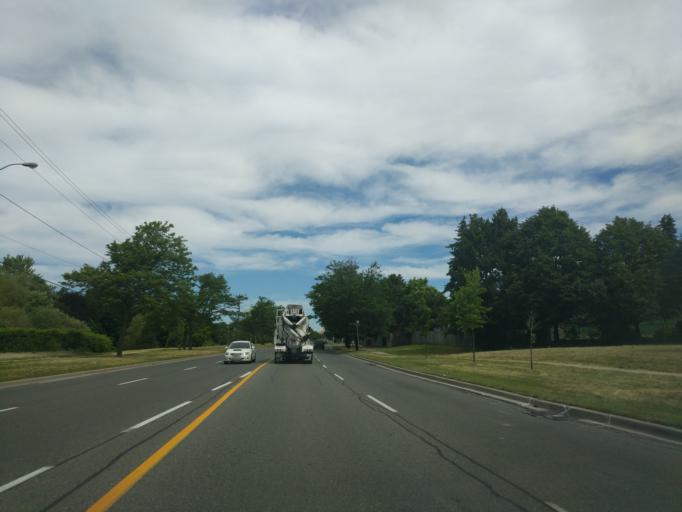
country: CA
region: Ontario
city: Scarborough
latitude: 43.7998
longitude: -79.2631
